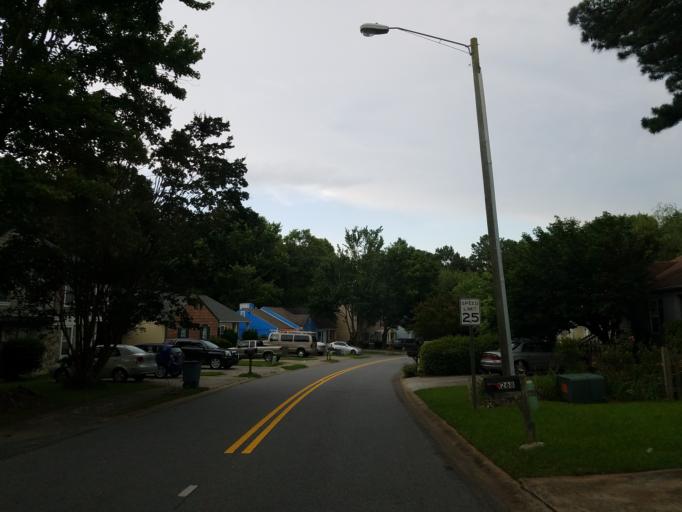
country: US
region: Georgia
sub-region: Cobb County
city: Fair Oaks
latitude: 33.9216
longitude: -84.5603
